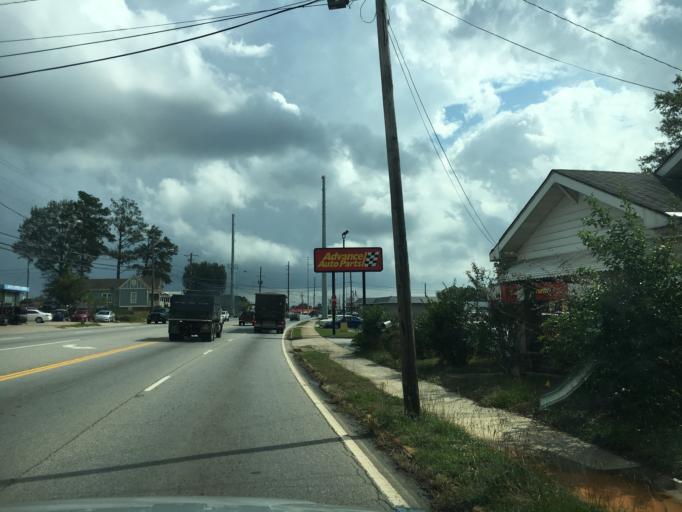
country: US
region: Georgia
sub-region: Elbert County
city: Elberton
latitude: 34.1070
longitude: -82.8562
